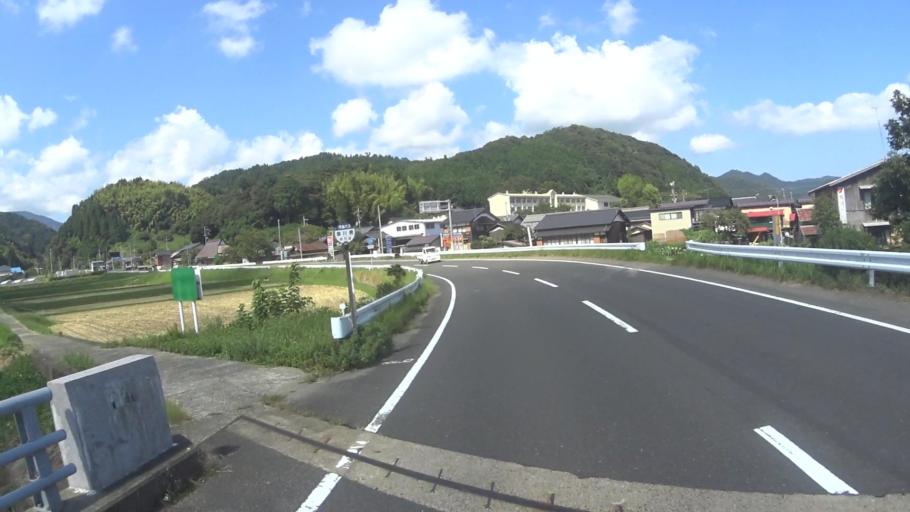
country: JP
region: Kyoto
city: Miyazu
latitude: 35.6565
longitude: 135.2588
